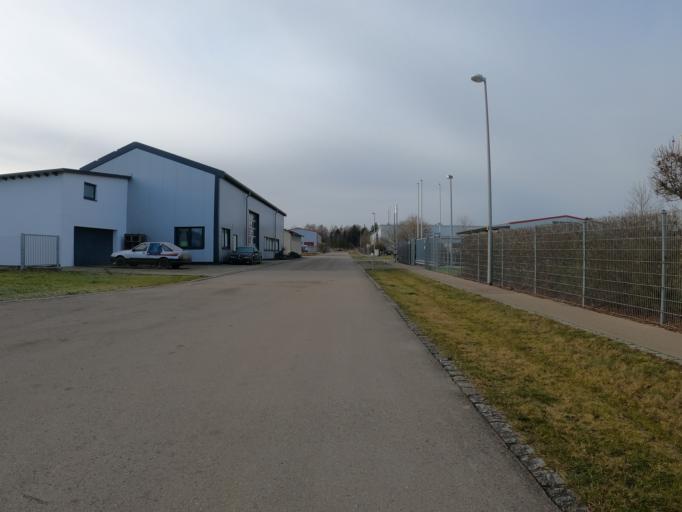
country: DE
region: Bavaria
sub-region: Swabia
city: Nersingen
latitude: 48.4191
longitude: 10.1761
